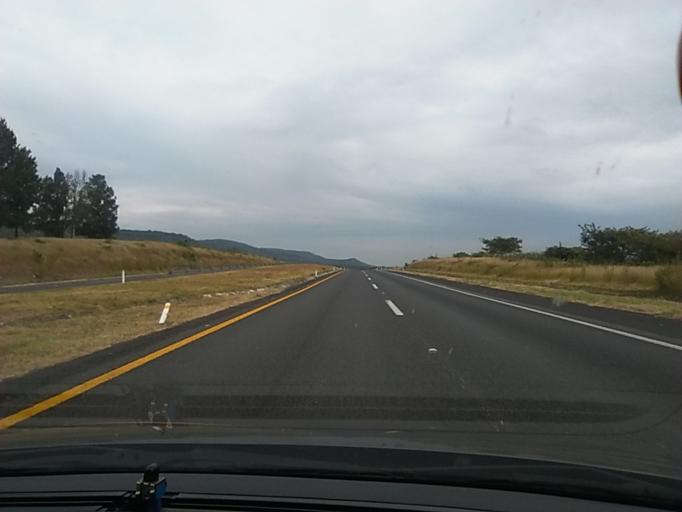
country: MX
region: Michoacan
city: Churintzio
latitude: 20.1236
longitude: -102.0573
